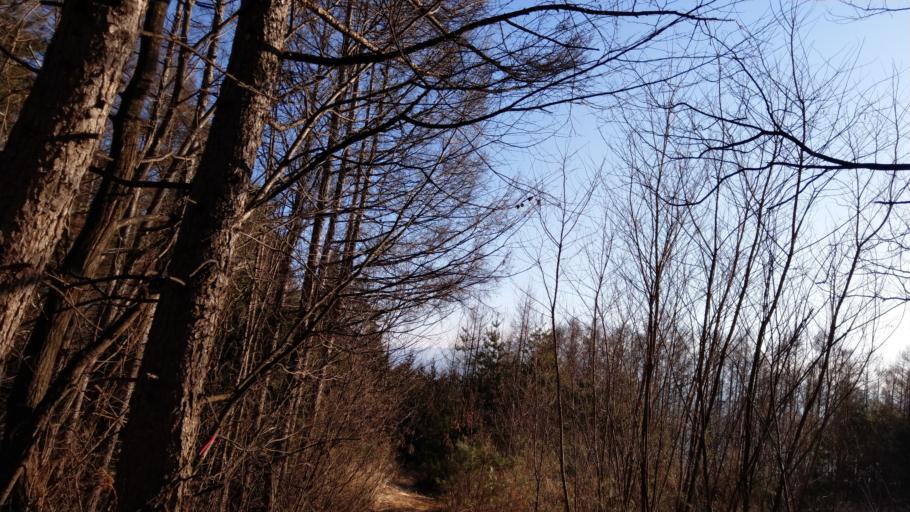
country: JP
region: Nagano
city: Komoro
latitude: 36.3651
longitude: 138.4313
